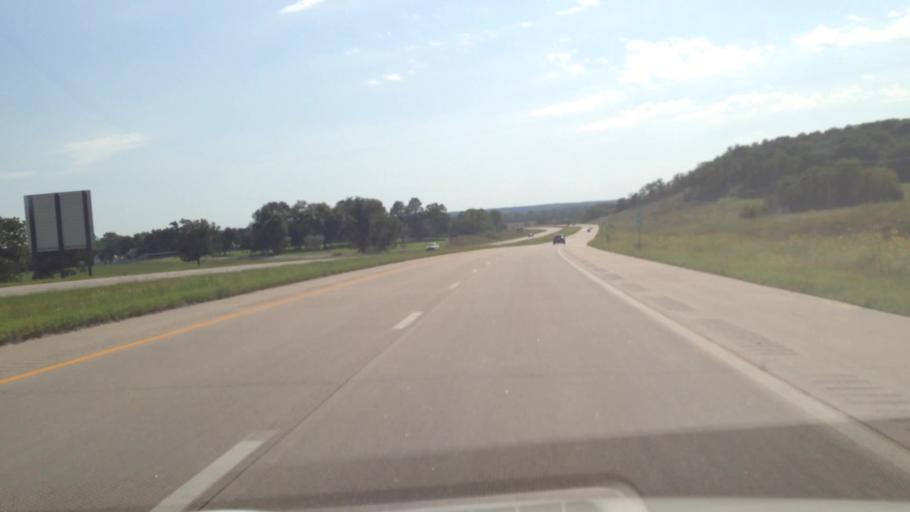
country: US
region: Kansas
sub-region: Linn County
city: Pleasanton
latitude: 38.2558
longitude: -94.6780
